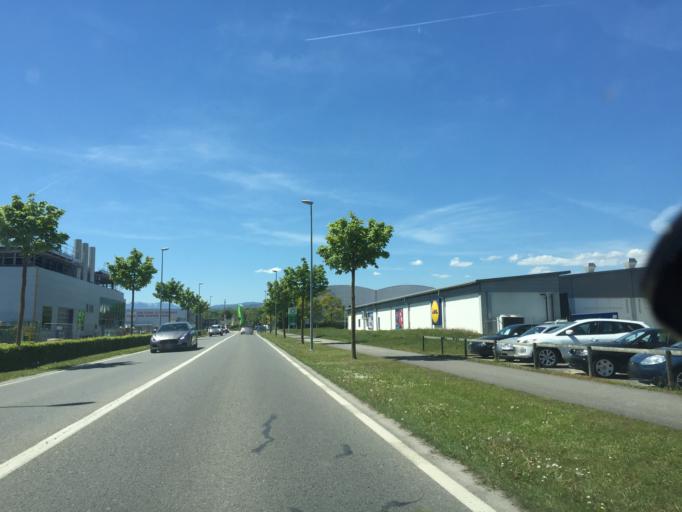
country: CH
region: Vaud
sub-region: Morges District
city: Aubonne
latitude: 46.4741
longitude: 6.4154
